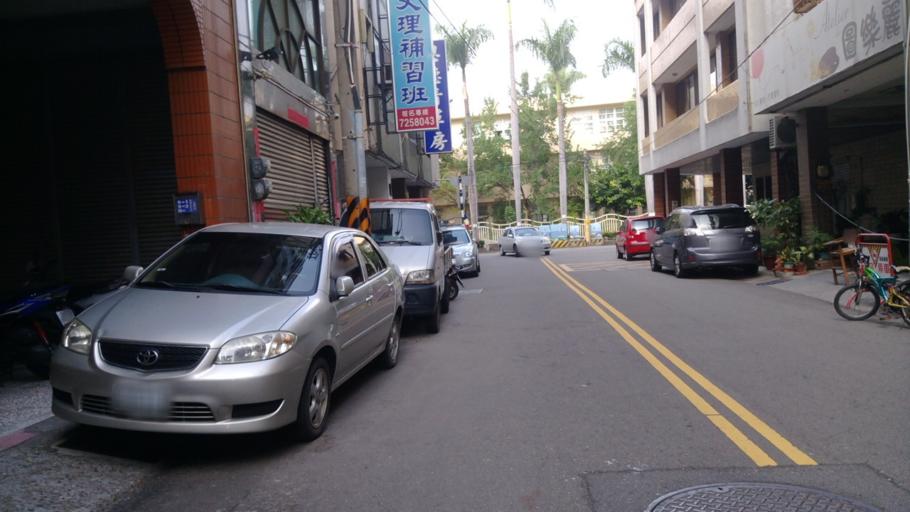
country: TW
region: Taiwan
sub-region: Changhua
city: Chang-hua
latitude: 24.0832
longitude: 120.5435
